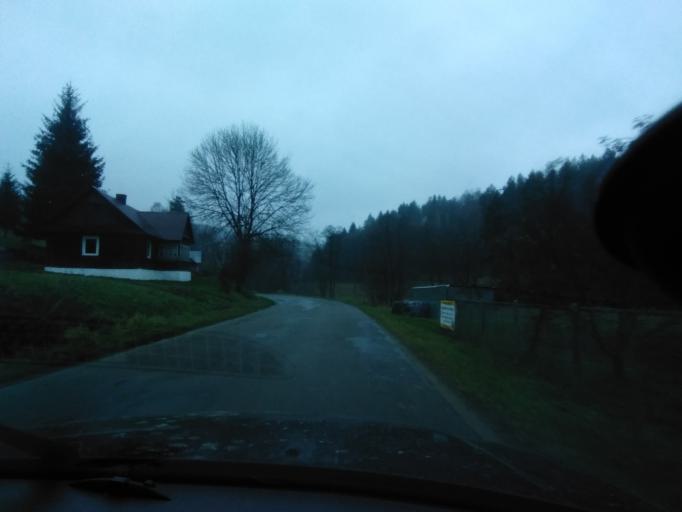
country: PL
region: Subcarpathian Voivodeship
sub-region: Powiat brzozowski
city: Nozdrzec
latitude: 49.7501
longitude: 22.1454
